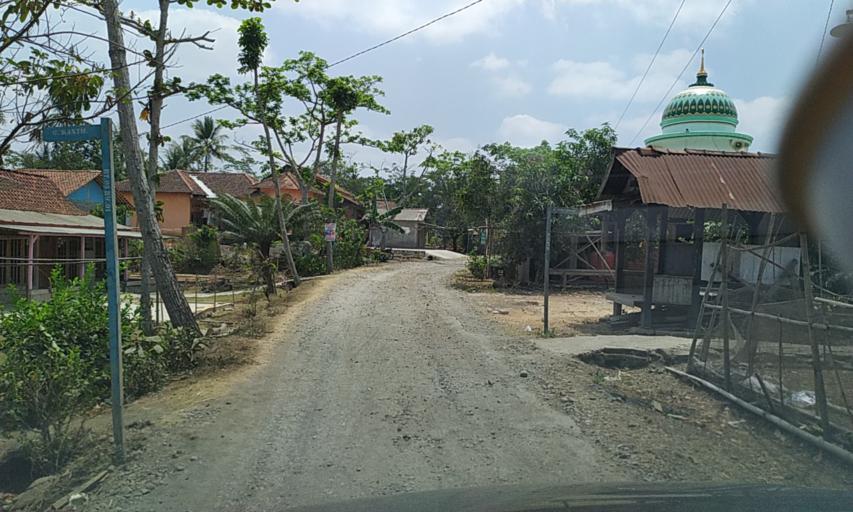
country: ID
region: Central Java
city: Prapagan
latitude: -7.5769
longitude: 108.9358
